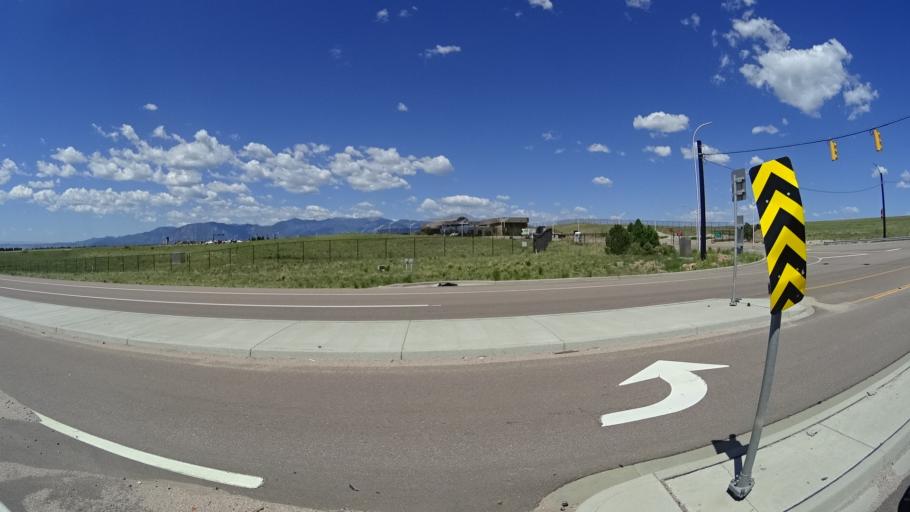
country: US
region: Colorado
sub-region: El Paso County
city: Cimarron Hills
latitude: 38.8260
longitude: -104.6827
